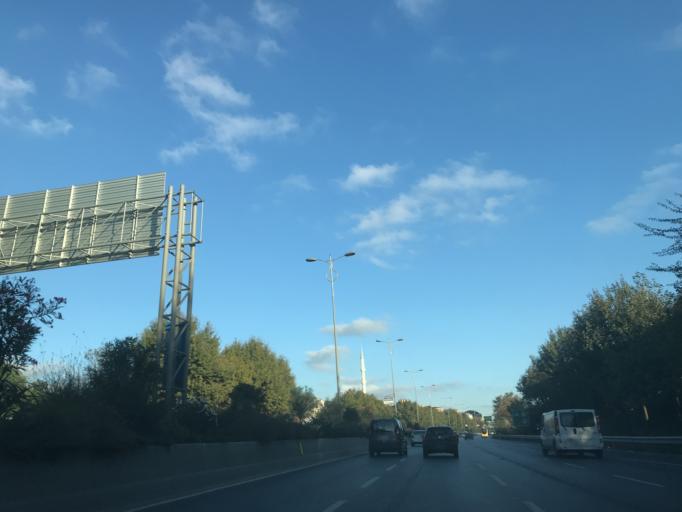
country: TR
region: Istanbul
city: Esenler
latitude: 41.0524
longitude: 28.8684
